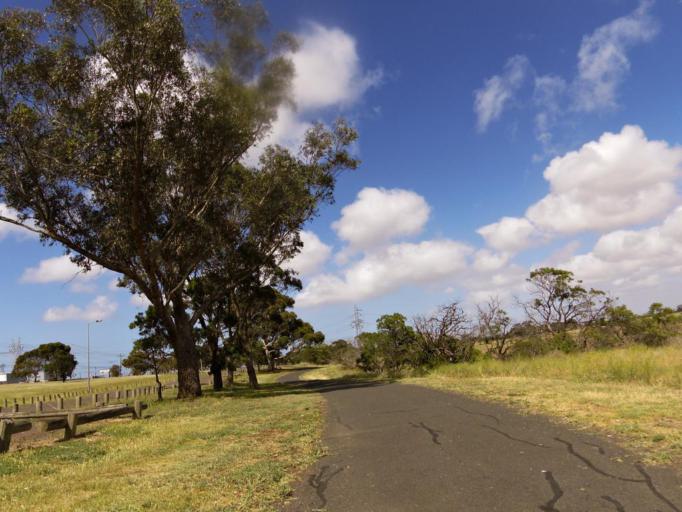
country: AU
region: Victoria
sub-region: Brimbank
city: Keilor Park
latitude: -37.7309
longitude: 144.8500
